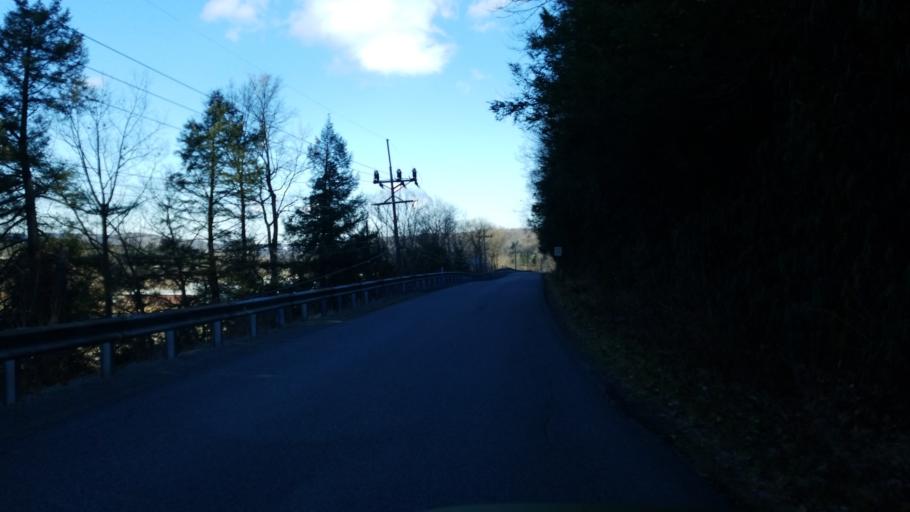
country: US
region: Pennsylvania
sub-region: Clearfield County
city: Hyde
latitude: 40.9859
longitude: -78.4758
